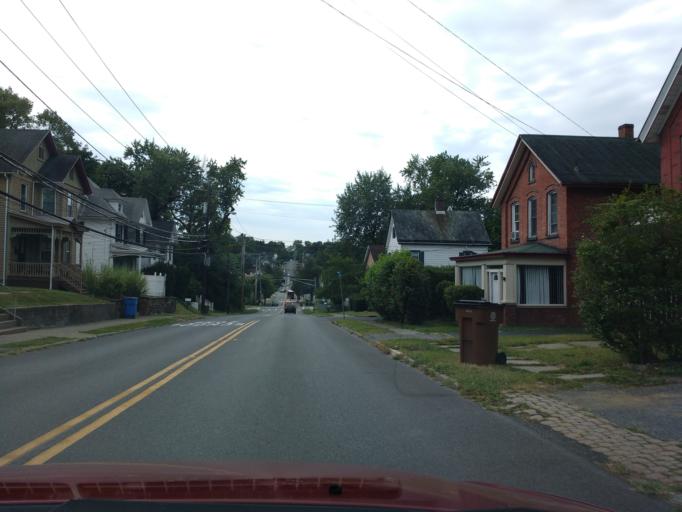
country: US
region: New York
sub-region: Ulster County
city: Kingston
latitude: 41.9279
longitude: -73.9910
